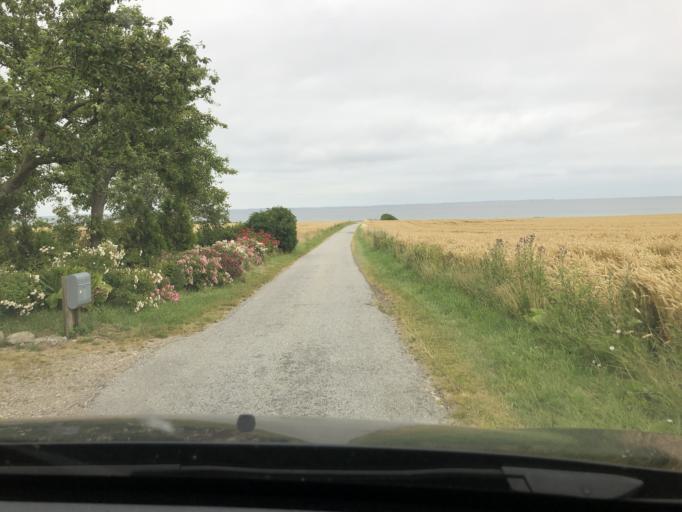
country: DK
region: South Denmark
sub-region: AEro Kommune
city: AEroskobing
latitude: 54.8317
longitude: 10.4343
